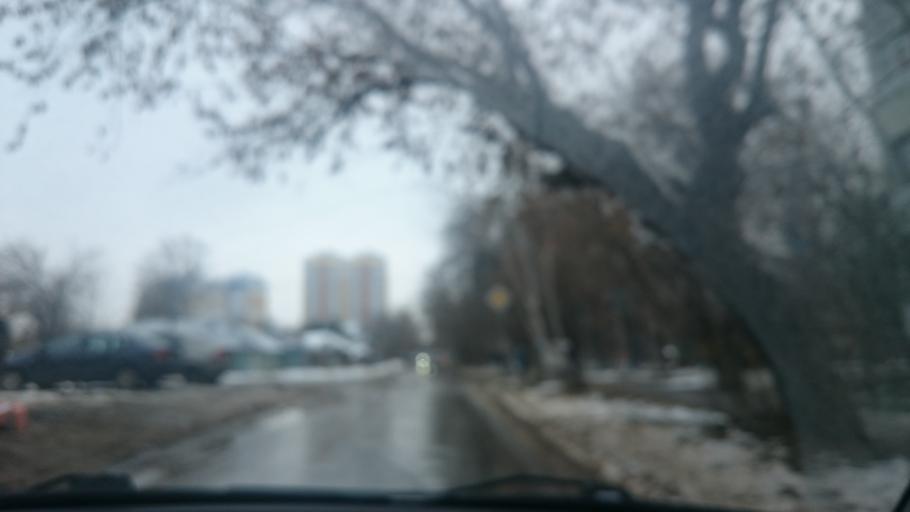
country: RU
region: Tula
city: Tula
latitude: 54.2127
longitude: 37.6091
